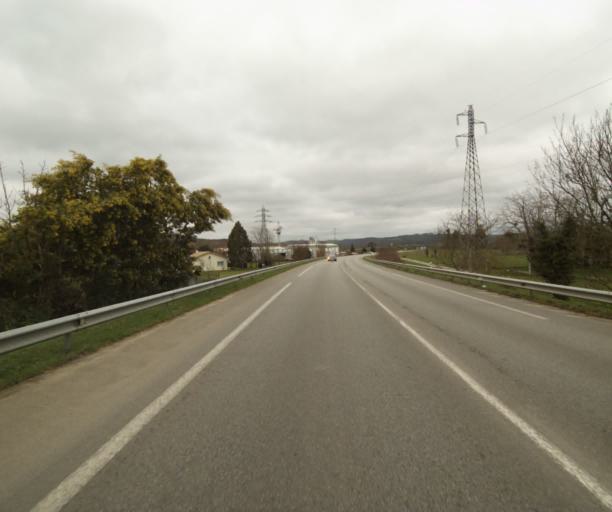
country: FR
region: Midi-Pyrenees
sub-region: Departement de l'Ariege
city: Pamiers
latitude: 43.1388
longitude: 1.6102
